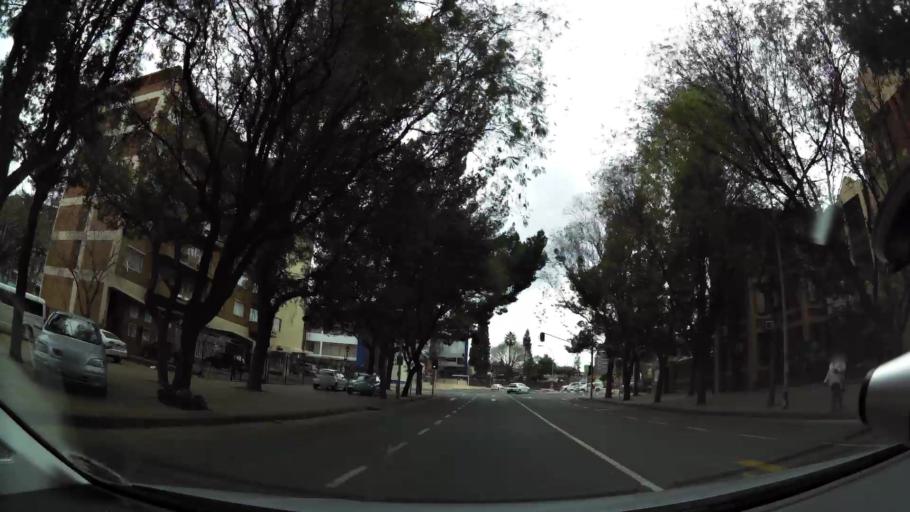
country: ZA
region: Orange Free State
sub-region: Mangaung Metropolitan Municipality
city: Bloemfontein
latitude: -29.1131
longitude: 26.2177
